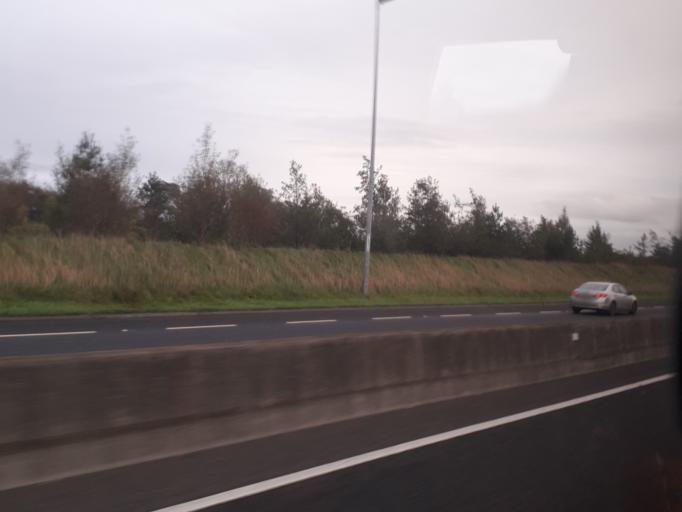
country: IE
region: Munster
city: Moyross
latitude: 52.6626
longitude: -8.6961
